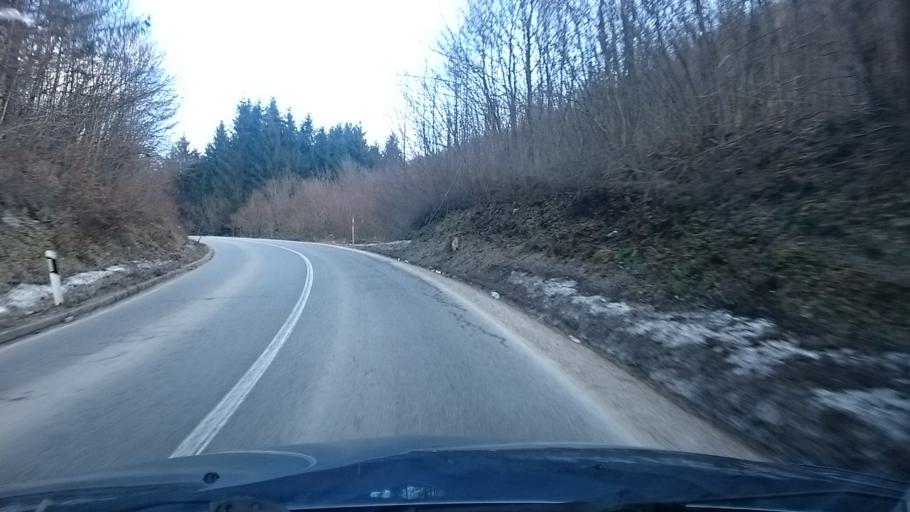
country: BA
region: Republika Srpska
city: Starcevica
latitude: 44.6729
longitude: 17.2197
